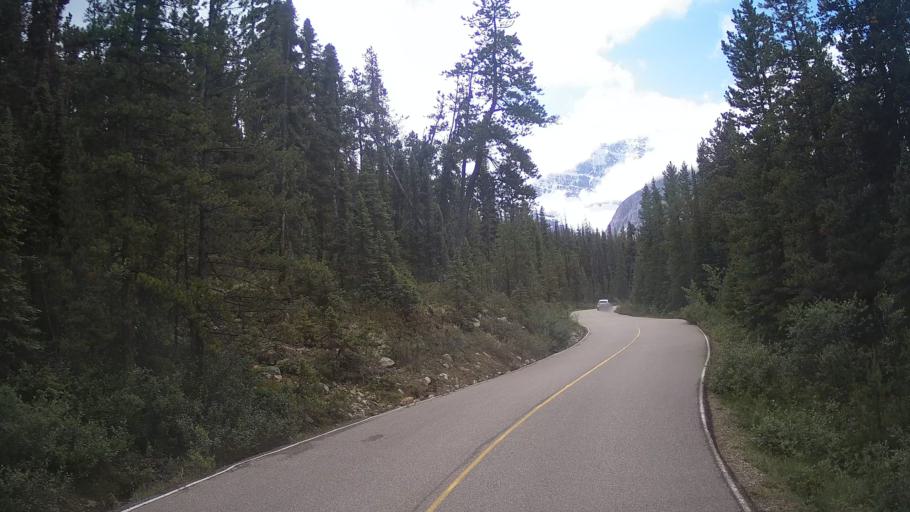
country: CA
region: Alberta
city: Jasper Park Lodge
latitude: 52.7217
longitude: -118.0516
